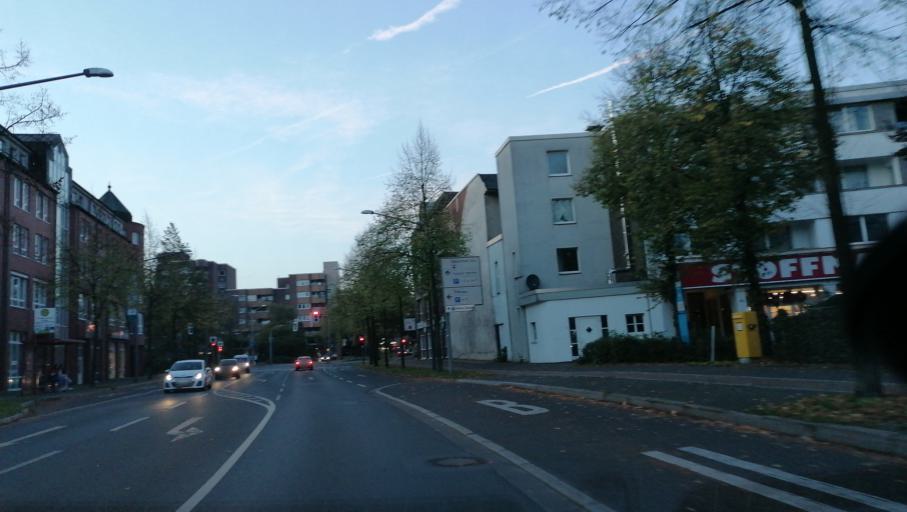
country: DE
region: North Rhine-Westphalia
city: Herten
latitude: 51.5905
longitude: 7.1420
